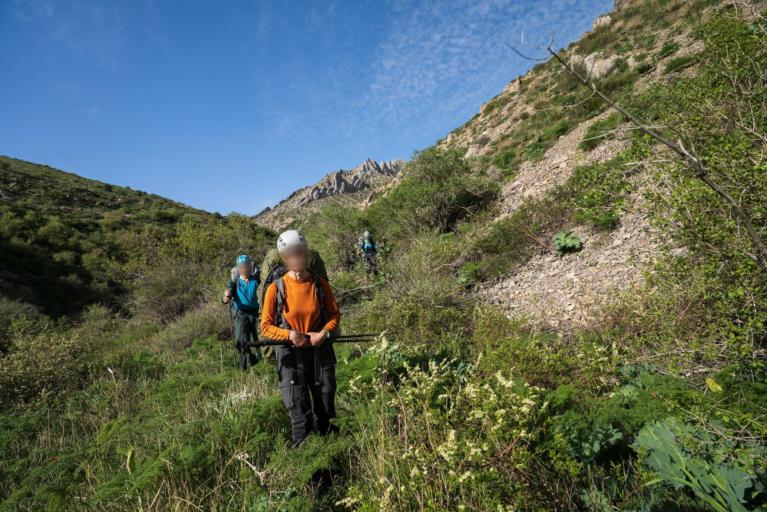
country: KZ
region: Ongtustik Qazaqstan
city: Ashchysay
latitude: 43.7686
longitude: 68.8093
